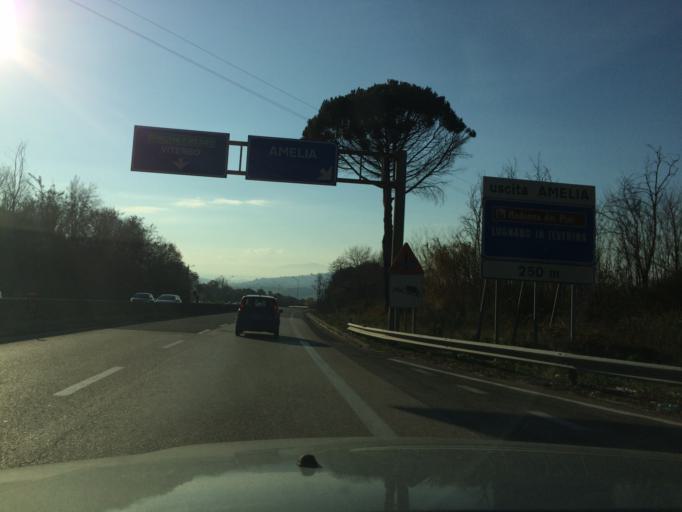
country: IT
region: Umbria
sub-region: Provincia di Terni
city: Fornole
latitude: 42.5321
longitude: 12.4768
